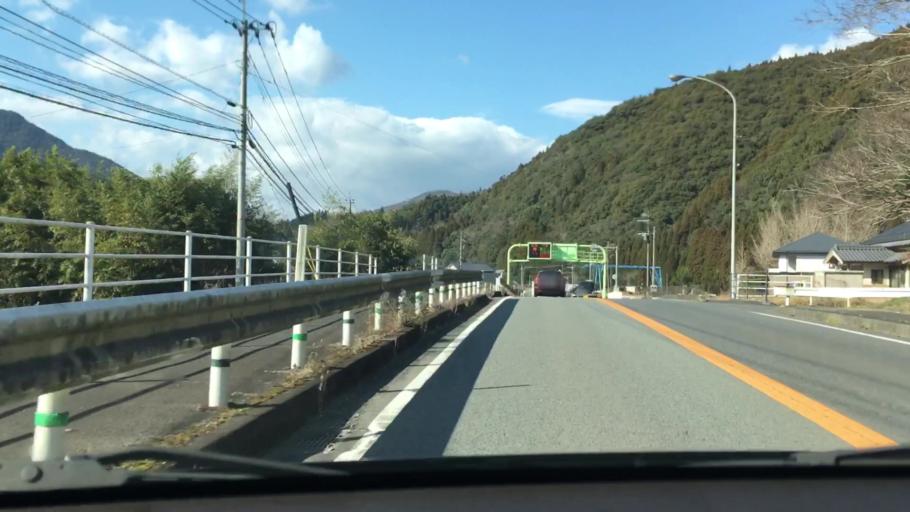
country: JP
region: Oita
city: Saiki
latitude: 32.9867
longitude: 131.8389
